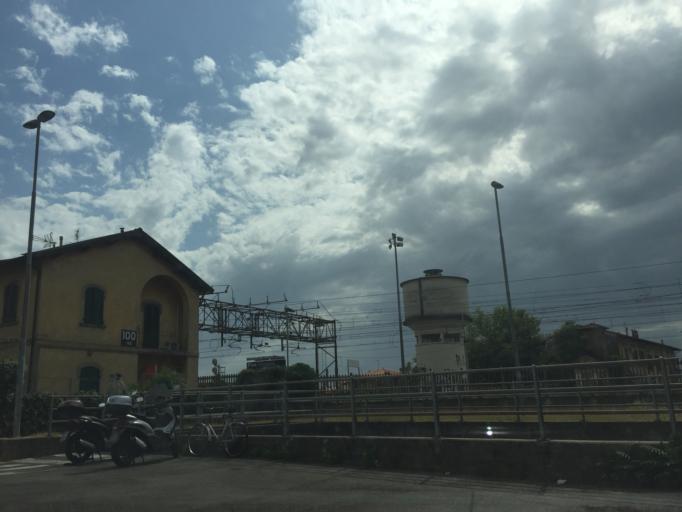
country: IT
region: Tuscany
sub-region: Province of Pisa
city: Madonna dell'Acqua
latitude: 43.7245
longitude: 10.3876
